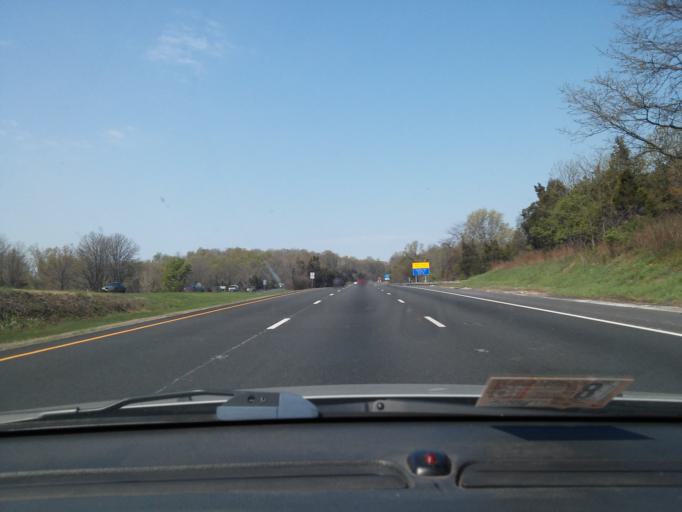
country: US
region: New Jersey
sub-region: Somerset County
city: Green Knoll
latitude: 40.6441
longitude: -74.6041
